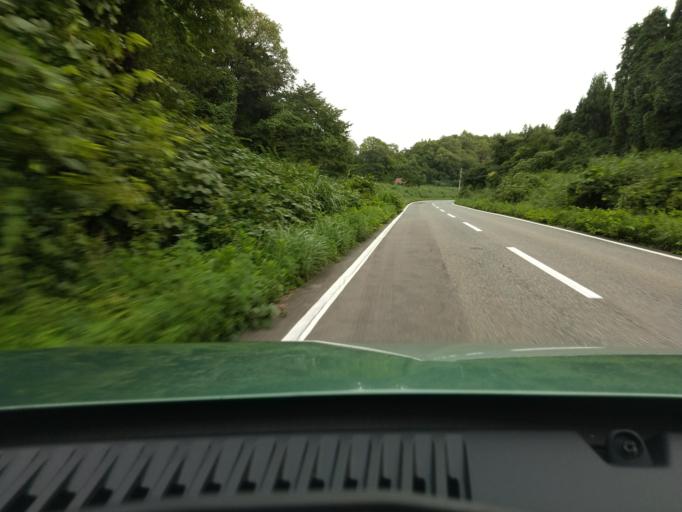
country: JP
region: Akita
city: Akita
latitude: 39.7289
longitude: 140.1826
